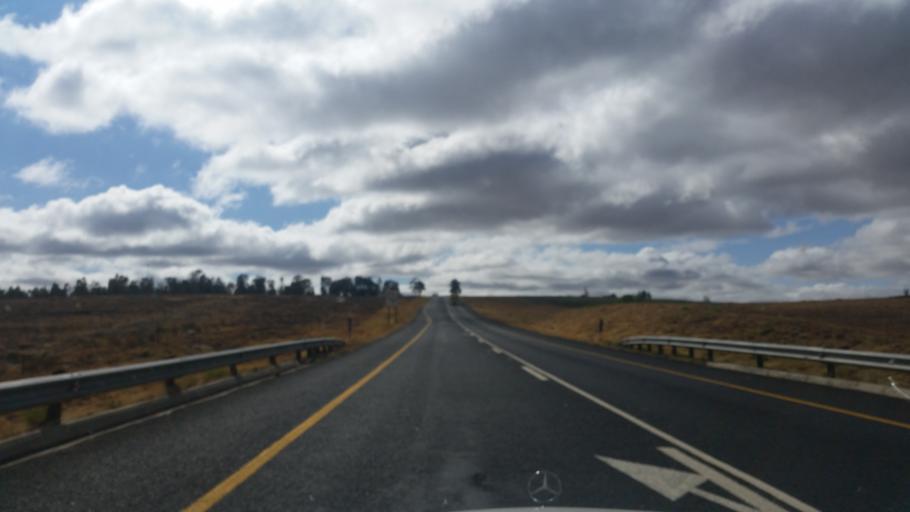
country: ZA
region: Orange Free State
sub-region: Thabo Mofutsanyana District Municipality
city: Phuthaditjhaba
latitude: -28.2958
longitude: 28.8052
